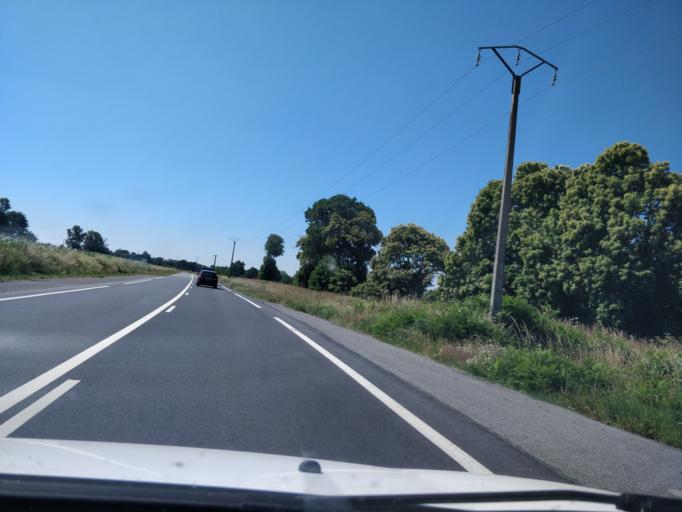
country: FR
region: Brittany
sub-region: Departement d'Ille-et-Vilaine
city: Dol-de-Bretagne
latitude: 48.5230
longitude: -1.7445
